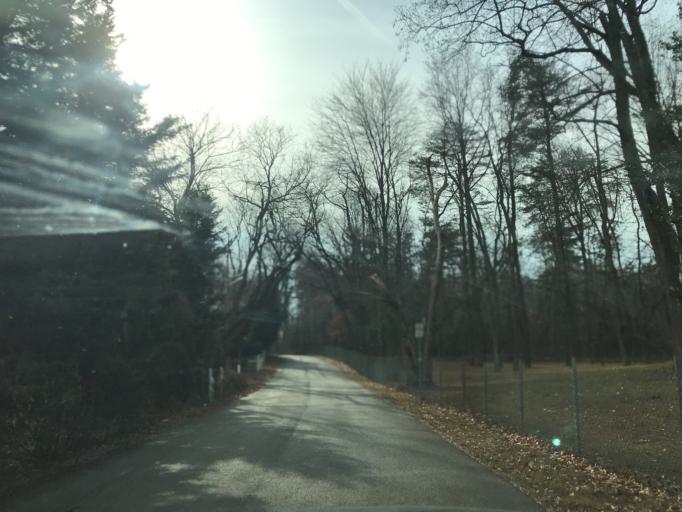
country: US
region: Maryland
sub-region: Howard County
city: Elkridge
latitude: 39.2117
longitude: -76.6895
